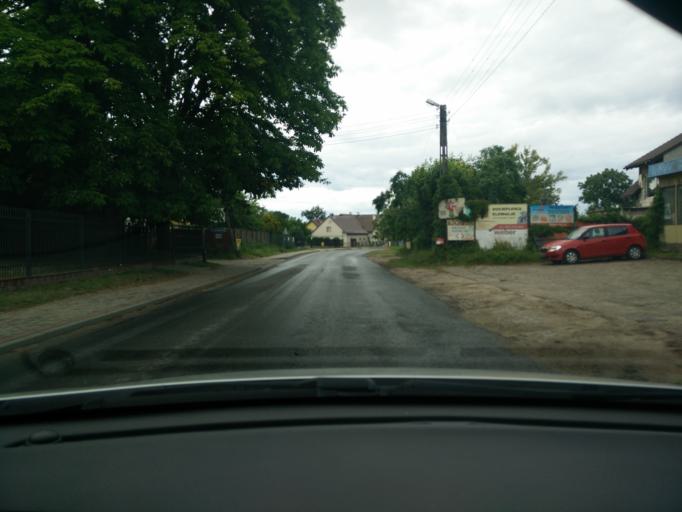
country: PL
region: Pomeranian Voivodeship
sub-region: Powiat pucki
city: Mosty
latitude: 54.6103
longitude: 18.4959
